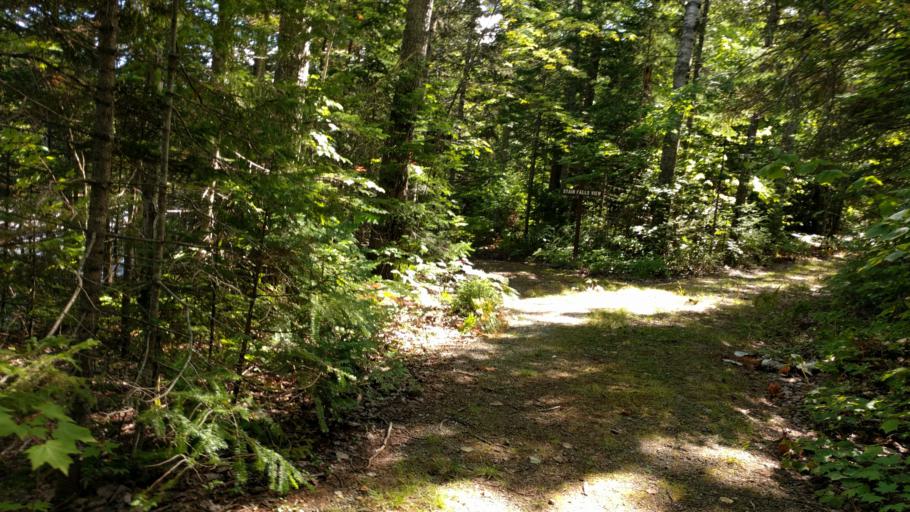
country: US
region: Maine
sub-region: Penobscot County
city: Patten
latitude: 46.0869
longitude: -68.7769
